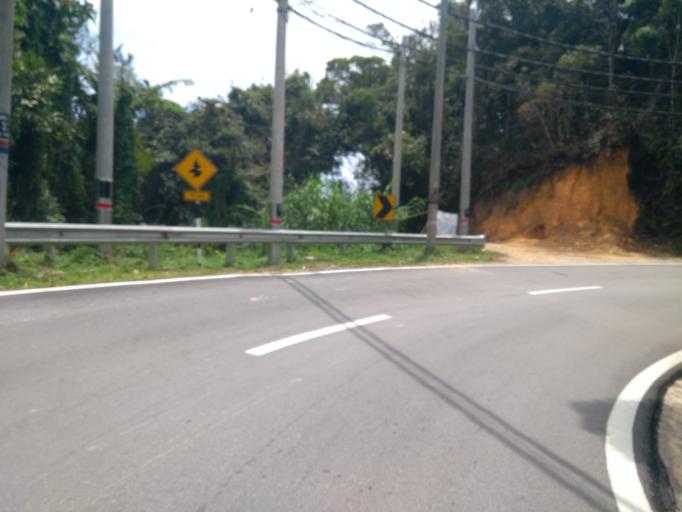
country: MY
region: Pahang
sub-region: Cameron Highlands
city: Tanah Rata
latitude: 4.4776
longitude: 101.3749
